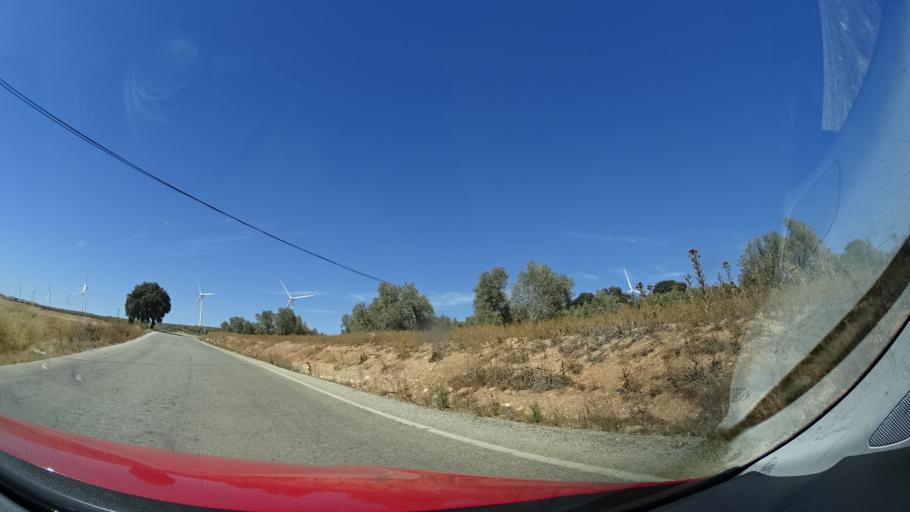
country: ES
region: Andalusia
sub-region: Provincia de Malaga
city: Sierra de Yeguas
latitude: 37.1000
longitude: -4.8688
